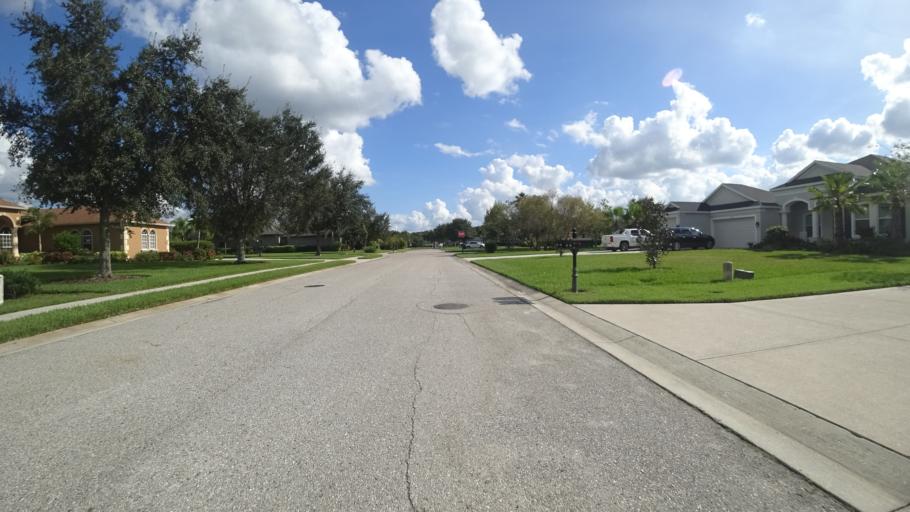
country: US
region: Florida
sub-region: Manatee County
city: Ellenton
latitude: 27.5431
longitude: -82.3784
